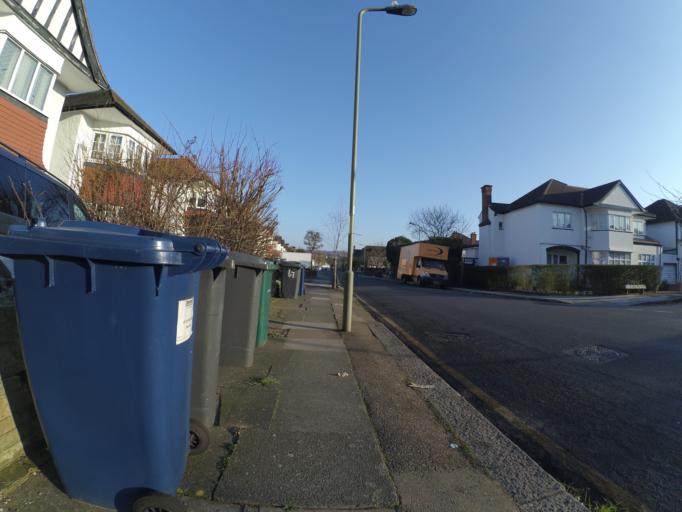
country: GB
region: England
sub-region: Greater London
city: Hendon
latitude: 51.5798
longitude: -0.2222
